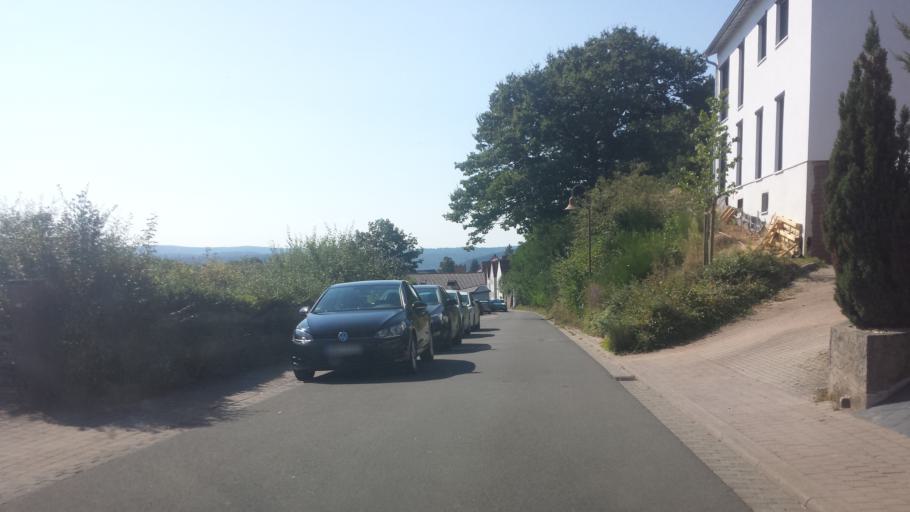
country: DE
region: Rheinland-Pfalz
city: Ramsen
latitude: 49.5532
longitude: 8.0299
